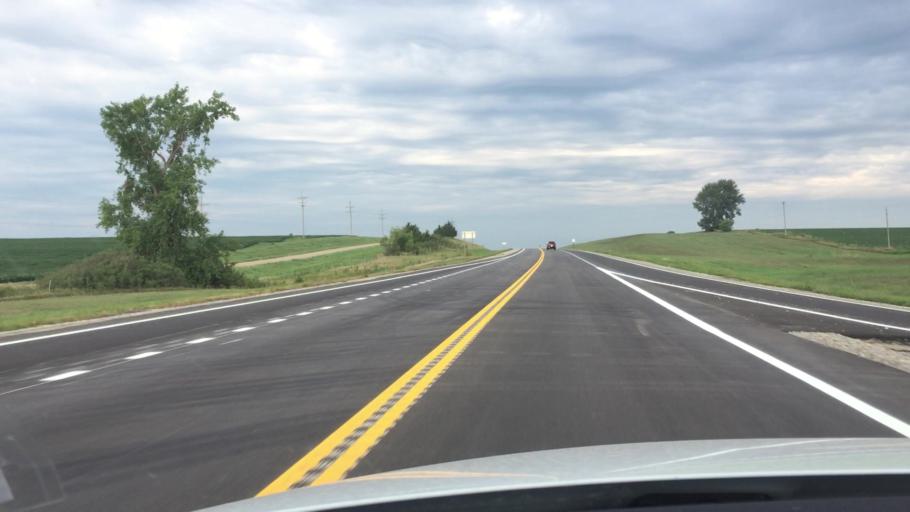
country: US
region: Kansas
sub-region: Brown County
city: Hiawatha
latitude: 39.8418
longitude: -95.4195
